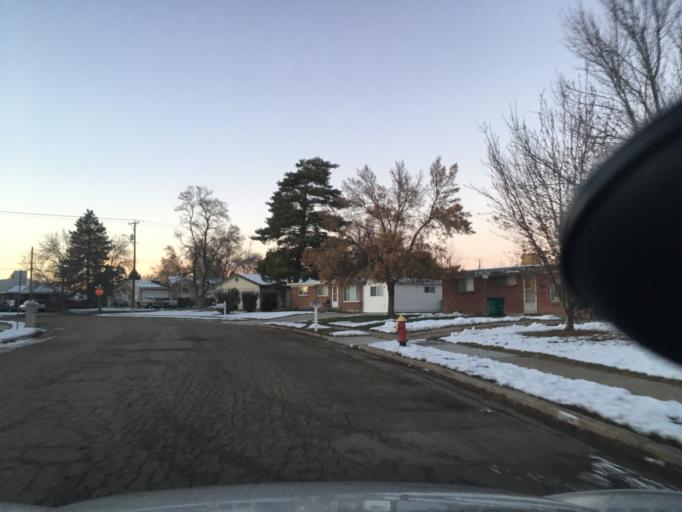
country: US
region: Utah
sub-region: Davis County
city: Layton
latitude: 41.0652
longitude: -111.9651
